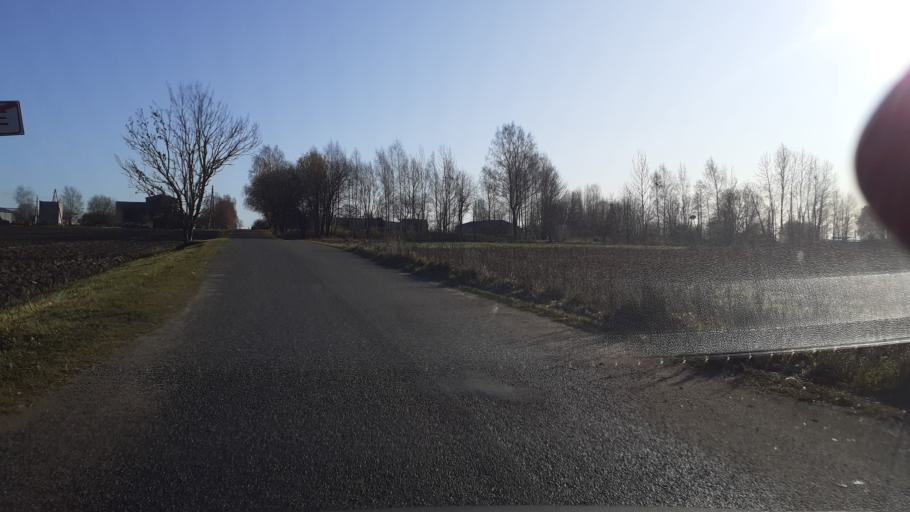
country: LV
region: Kuldigas Rajons
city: Kuldiga
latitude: 56.9979
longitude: 21.8913
